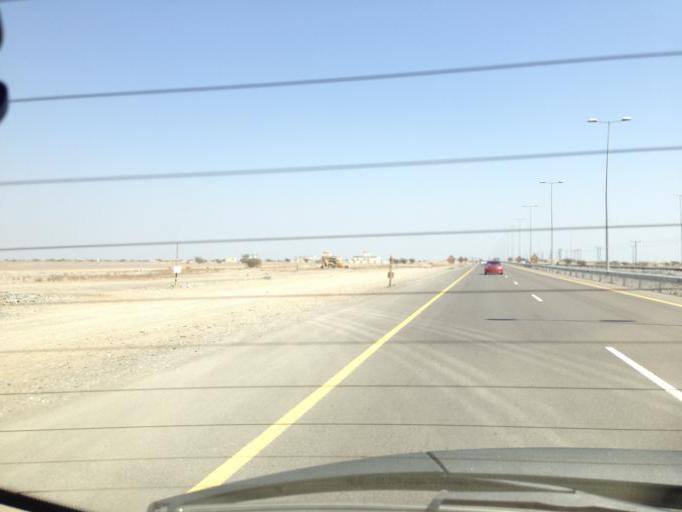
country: OM
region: Al Batinah
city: Rustaq
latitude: 23.5804
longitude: 57.4936
